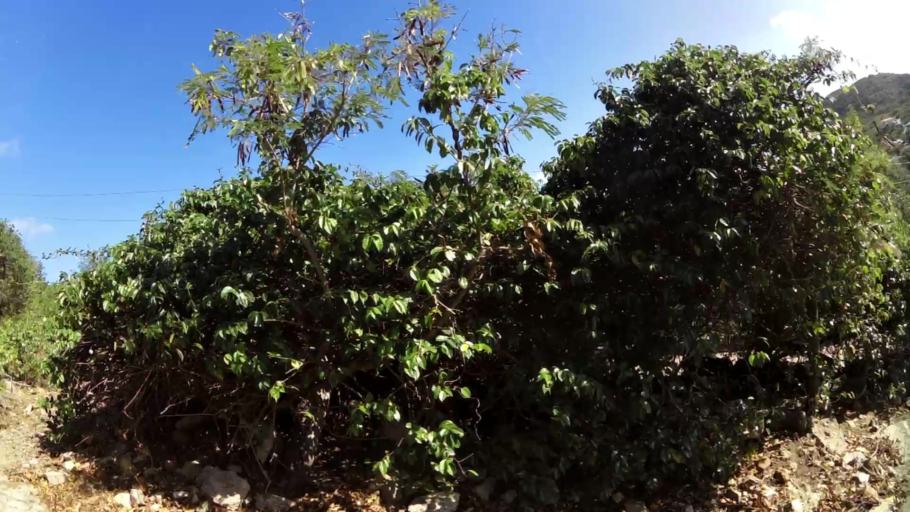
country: VG
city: Tortola
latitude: 18.4868
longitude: -64.3859
